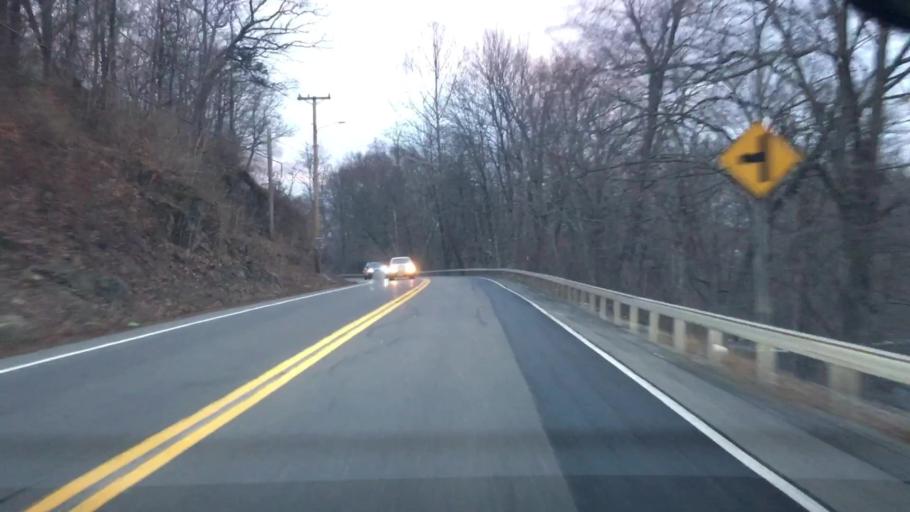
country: US
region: New York
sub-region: Dutchess County
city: Red Oaks Mill
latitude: 41.6660
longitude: -73.8776
